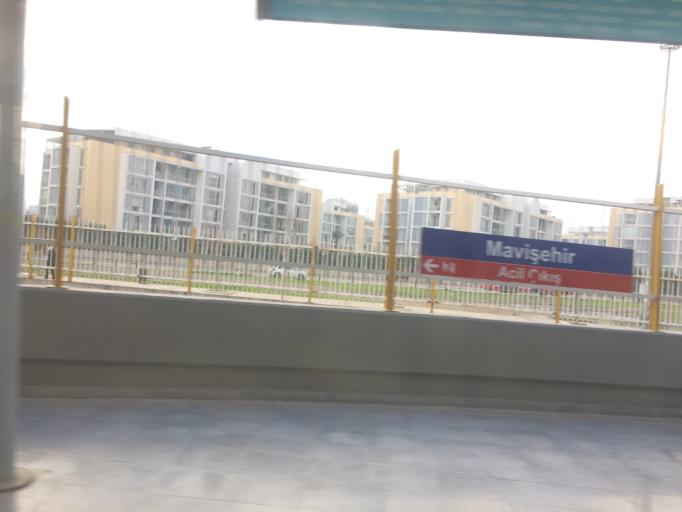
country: TR
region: Izmir
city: Karsiyaka
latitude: 38.4819
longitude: 27.0830
